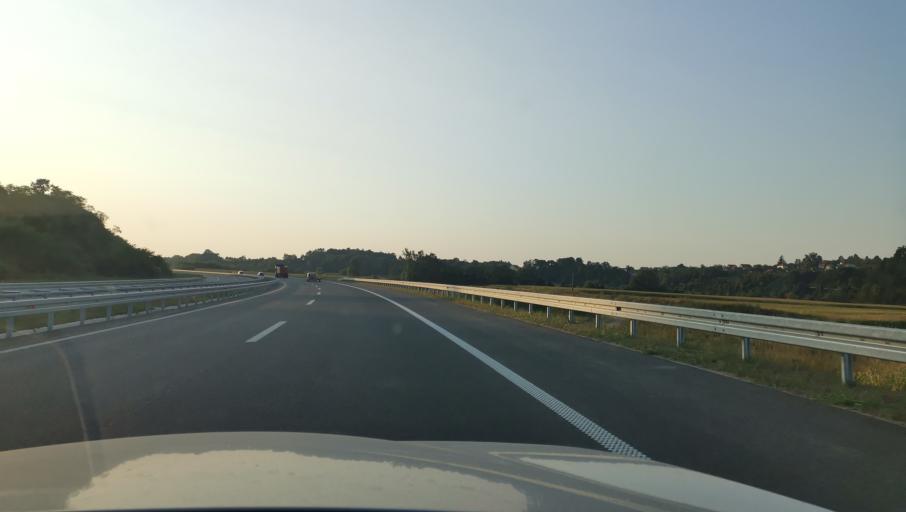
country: RS
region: Central Serbia
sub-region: Kolubarski Okrug
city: Lajkovac
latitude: 44.3405
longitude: 20.1966
